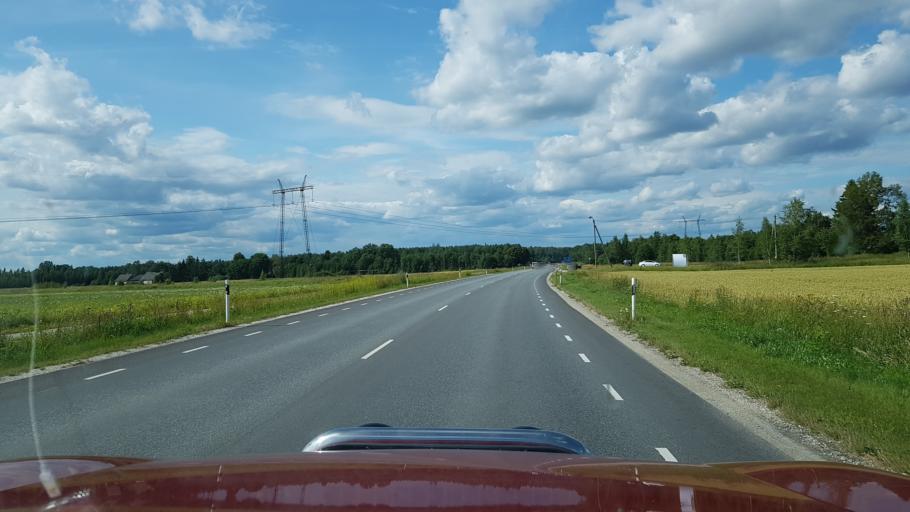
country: EE
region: Tartu
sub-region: Tartu linn
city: Tartu
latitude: 58.4496
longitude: 26.6760
